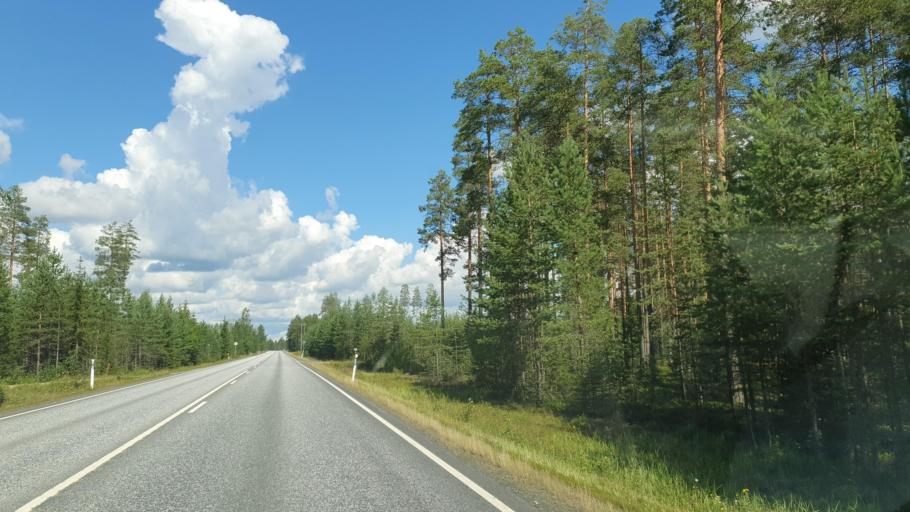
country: FI
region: Northern Savo
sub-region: Ylae-Savo
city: Sonkajaervi
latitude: 63.8241
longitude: 27.4210
